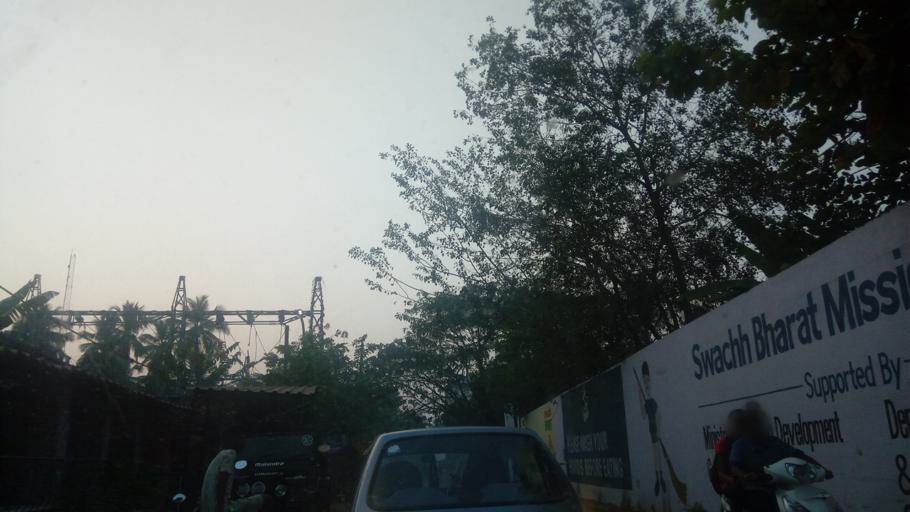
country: IN
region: Goa
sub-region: South Goa
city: Madgaon
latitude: 15.2883
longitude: 73.9618
